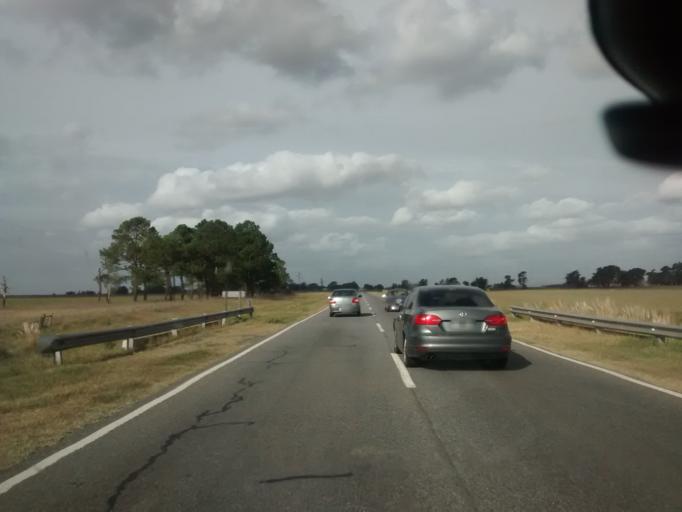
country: AR
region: Buenos Aires
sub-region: Partido de Balcarce
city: Balcarce
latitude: -37.6718
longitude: -58.4706
